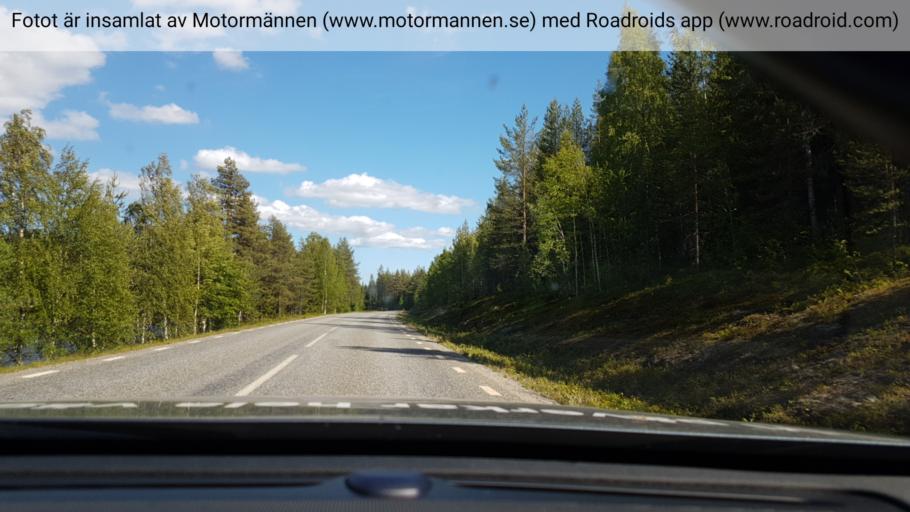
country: SE
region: Vaesterbotten
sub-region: Lycksele Kommun
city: Lycksele
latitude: 64.6146
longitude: 18.4657
